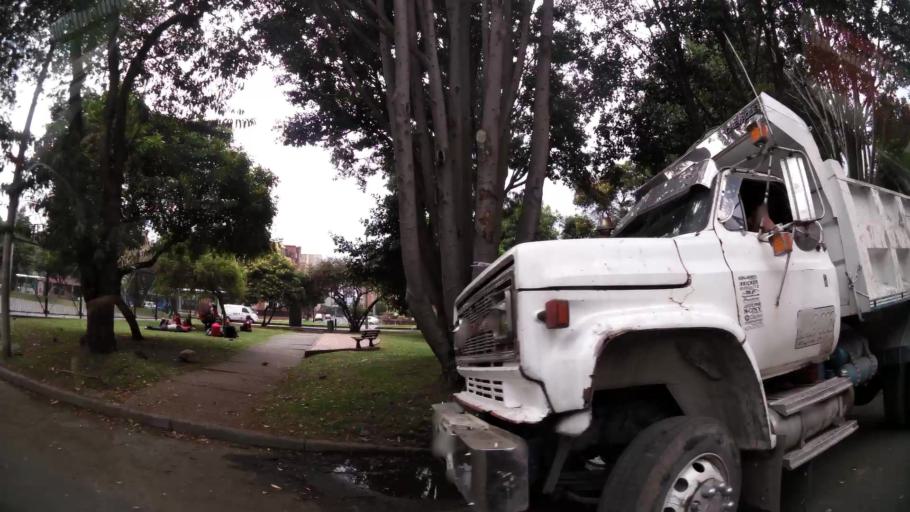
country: CO
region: Bogota D.C.
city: Barrio San Luis
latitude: 4.7276
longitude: -74.0452
